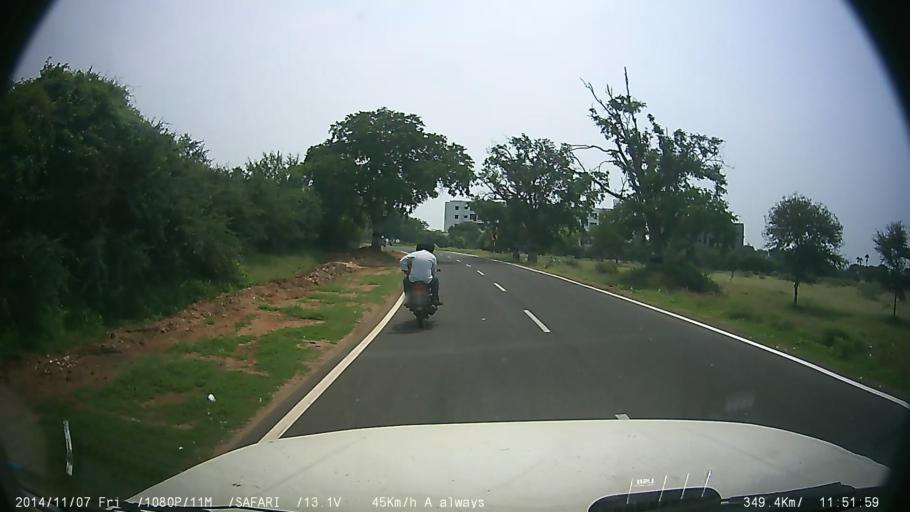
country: IN
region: Tamil Nadu
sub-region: Tiruppur
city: Avinashi
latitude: 11.1407
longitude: 77.2651
